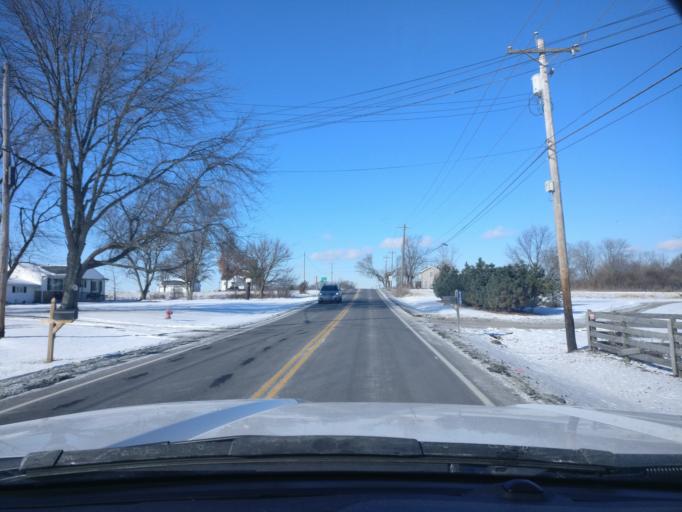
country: US
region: Ohio
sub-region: Warren County
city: Hunter
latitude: 39.4992
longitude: -84.2584
